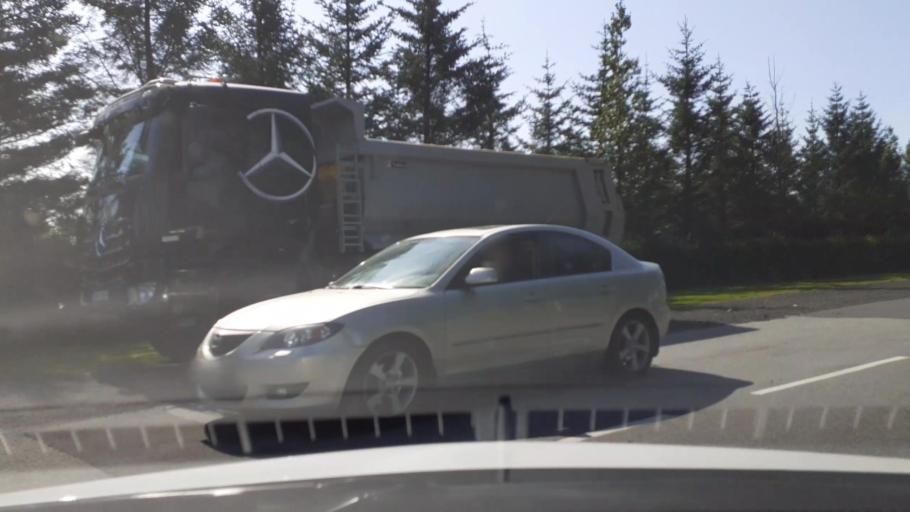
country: IS
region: South
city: Selfoss
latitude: 63.9338
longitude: -20.9872
